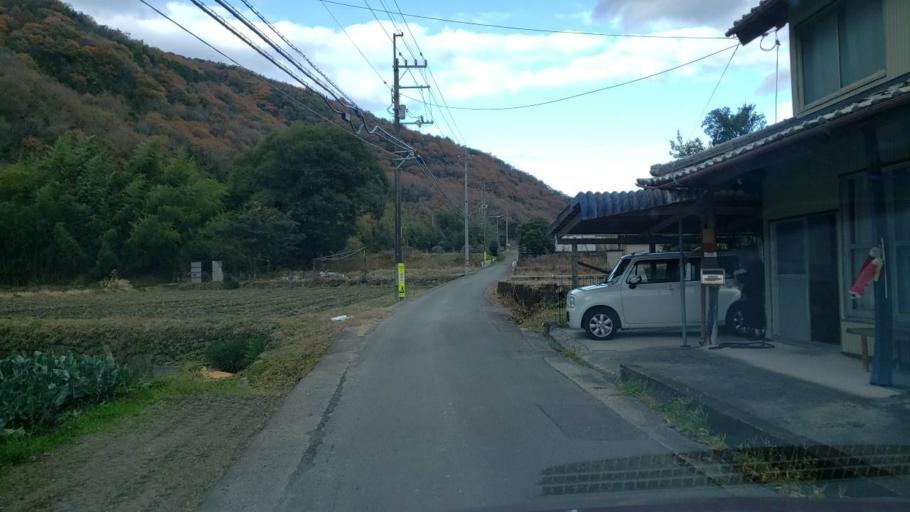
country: JP
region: Tokushima
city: Wakimachi
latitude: 34.1097
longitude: 134.2241
